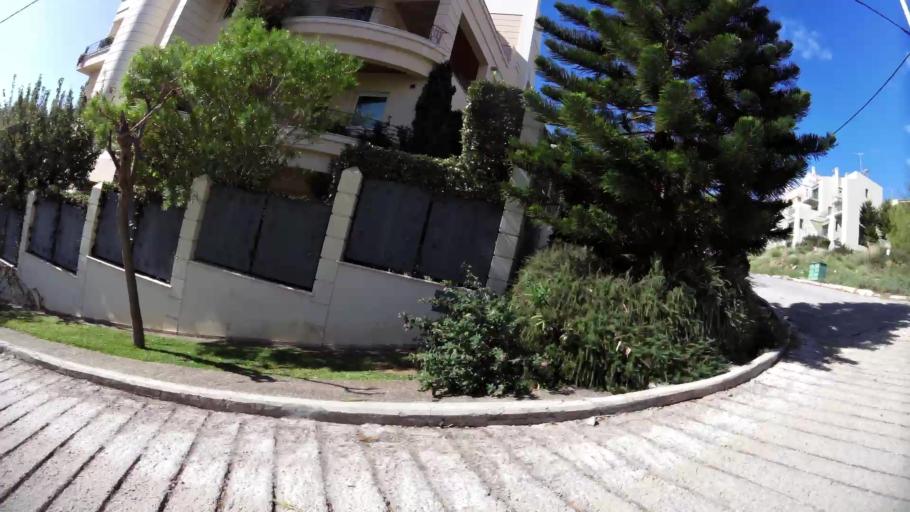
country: GR
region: Attica
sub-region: Nomarchia Anatolikis Attikis
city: Voula
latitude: 37.8450
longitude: 23.7845
